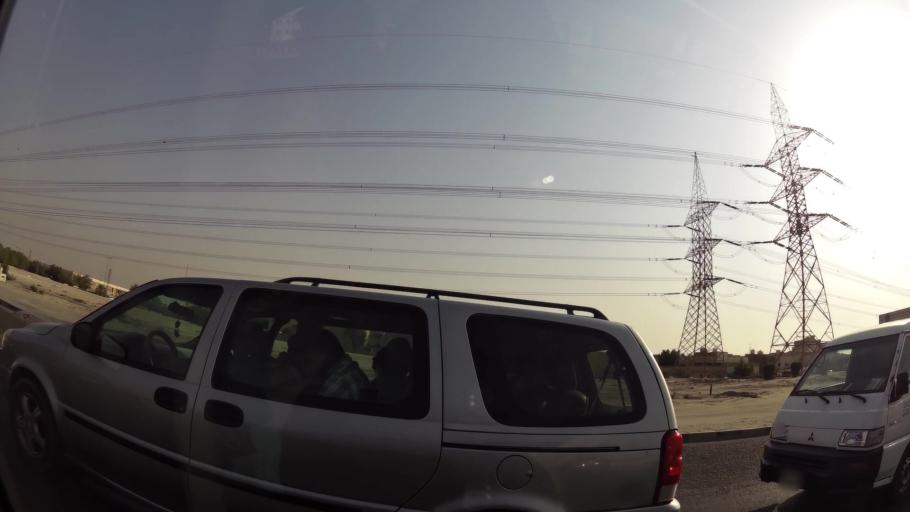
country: KW
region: Al Asimah
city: Ar Rabiyah
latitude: 29.2965
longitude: 47.8773
